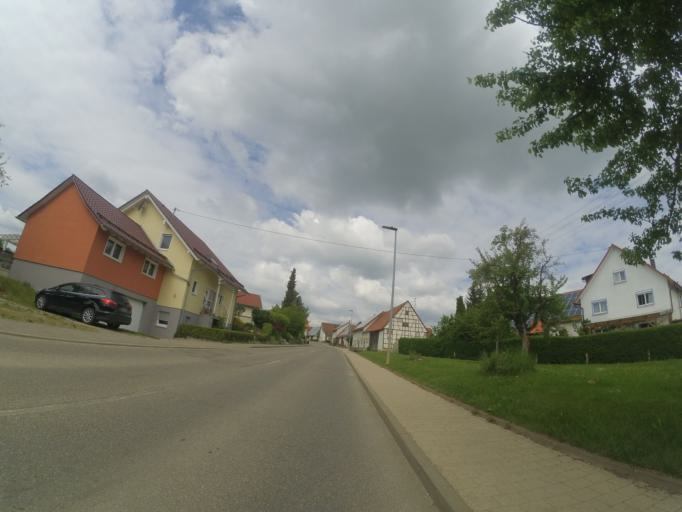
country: DE
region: Baden-Wuerttemberg
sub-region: Tuebingen Region
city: Berghulen
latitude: 48.4634
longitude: 9.7651
